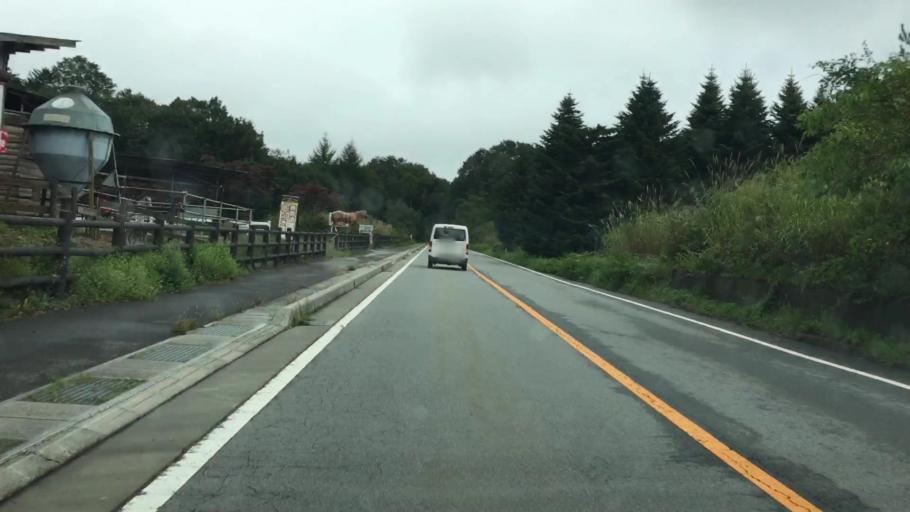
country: JP
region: Yamanashi
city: Fujikawaguchiko
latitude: 35.4743
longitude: 138.6771
